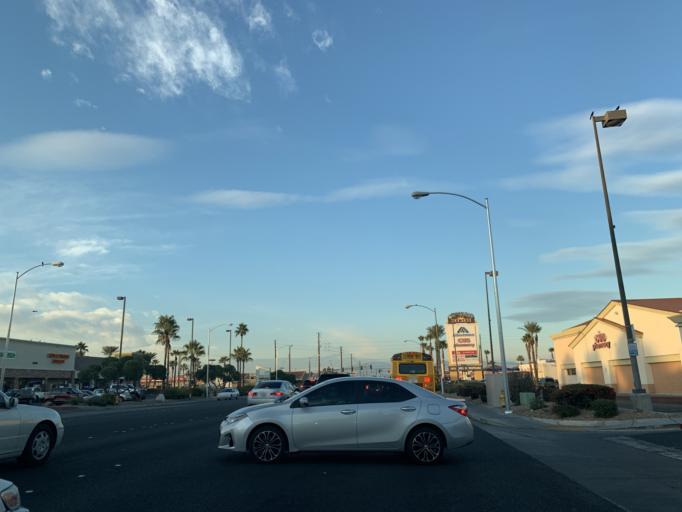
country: US
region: Nevada
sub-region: Clark County
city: Spring Valley
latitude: 36.0981
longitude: -115.2249
